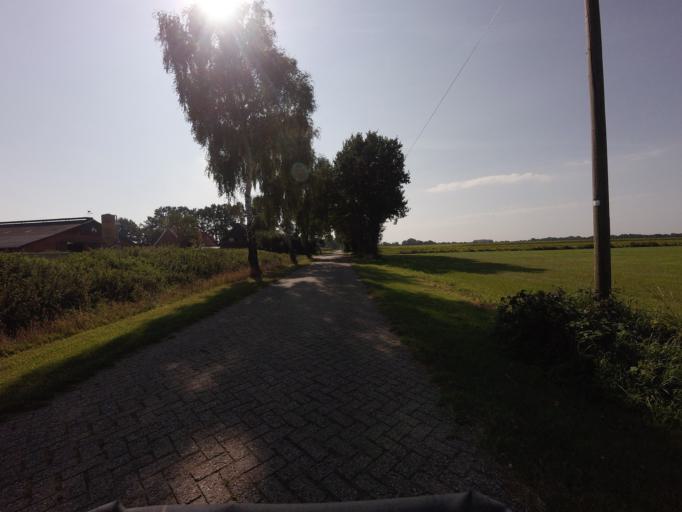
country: DE
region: Lower Saxony
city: Emlichheim
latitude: 52.5867
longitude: 6.8339
